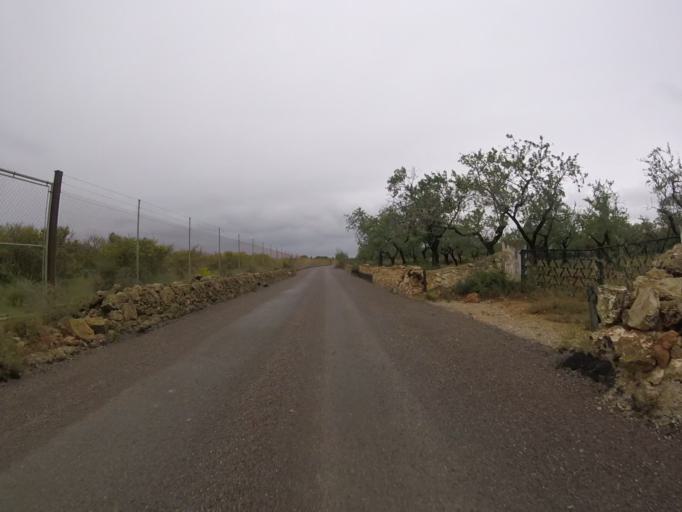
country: ES
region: Valencia
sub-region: Provincia de Castello
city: Alcoceber
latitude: 40.2371
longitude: 0.2527
